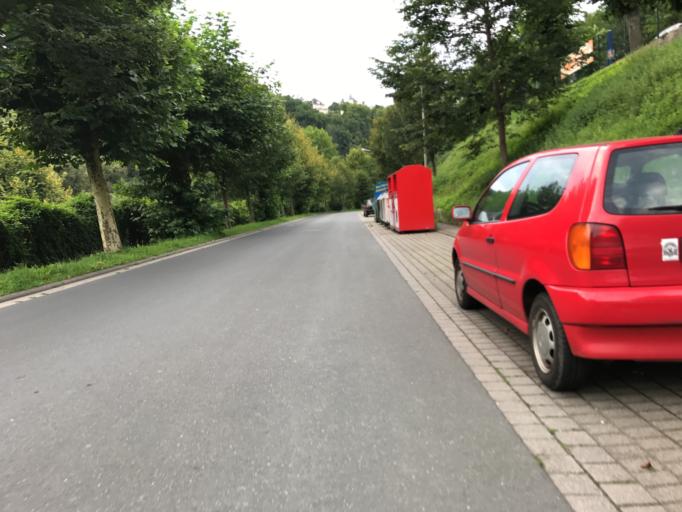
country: DE
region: Hesse
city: Weilburg
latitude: 50.4848
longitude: 8.2580
